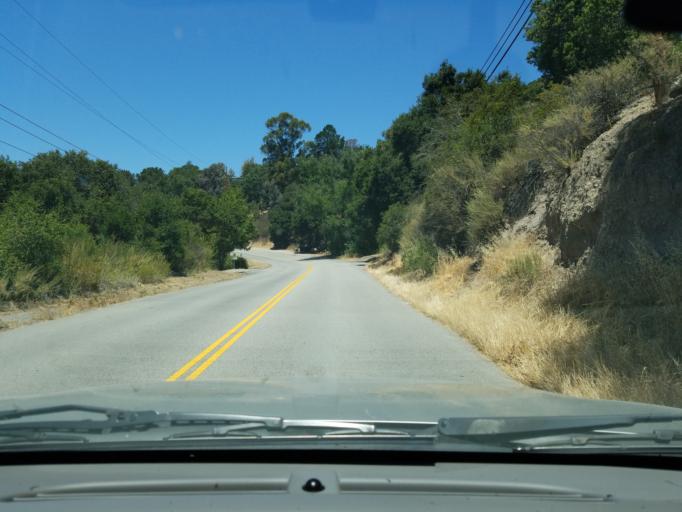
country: US
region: California
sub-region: Monterey County
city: Carmel Valley Village
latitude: 36.4750
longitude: -121.7186
